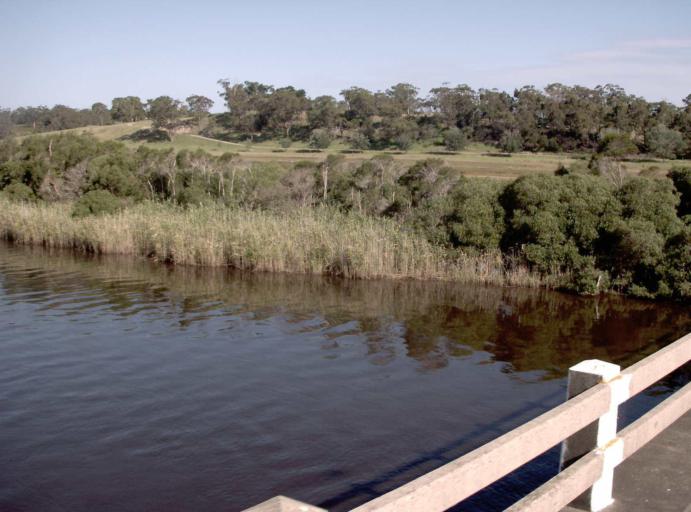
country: AU
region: Victoria
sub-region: East Gippsland
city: Lakes Entrance
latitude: -37.7788
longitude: 148.5390
